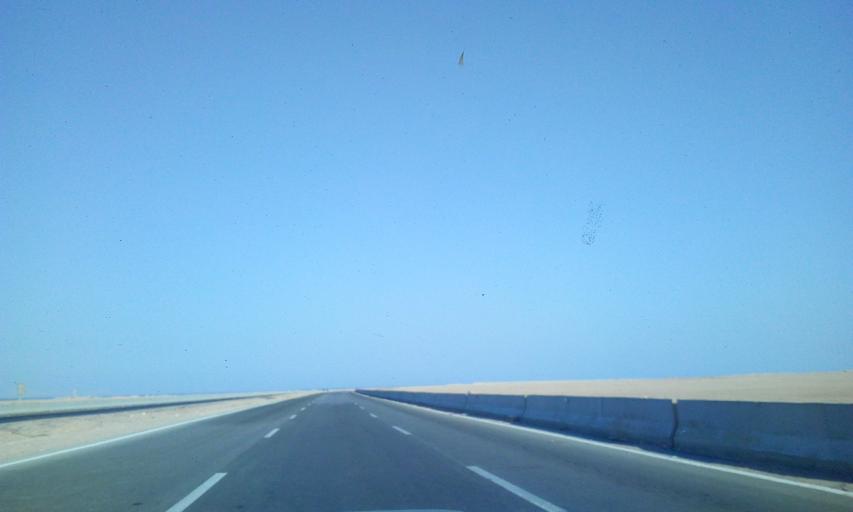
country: EG
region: As Suways
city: Ain Sukhna
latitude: 29.1084
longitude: 32.5986
